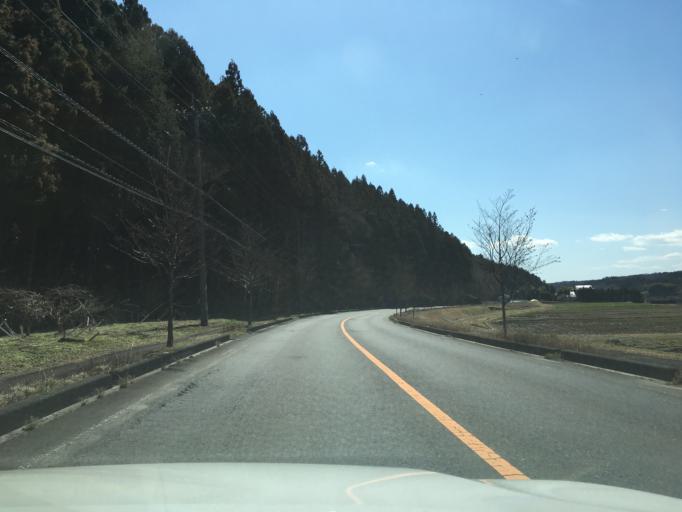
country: JP
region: Tochigi
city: Kuroiso
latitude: 36.9480
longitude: 140.1477
